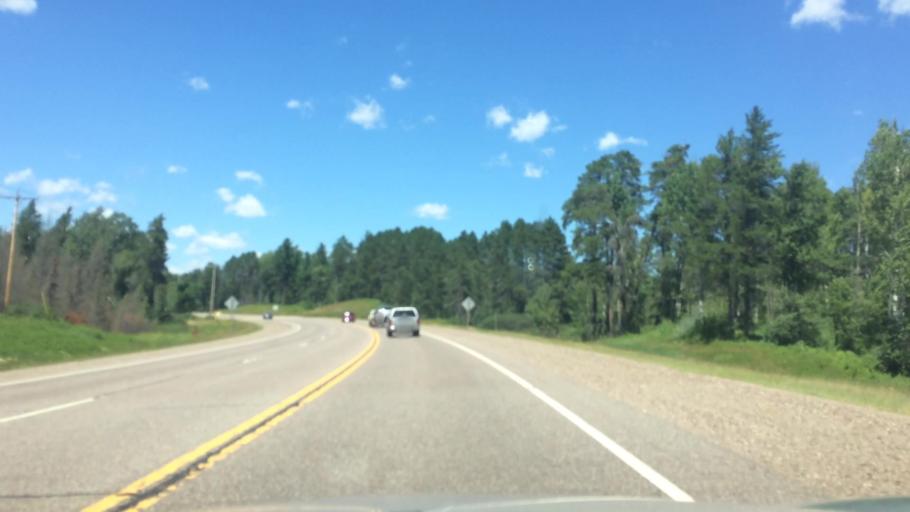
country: US
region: Wisconsin
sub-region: Lincoln County
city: Tomahawk
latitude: 45.6554
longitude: -89.7049
